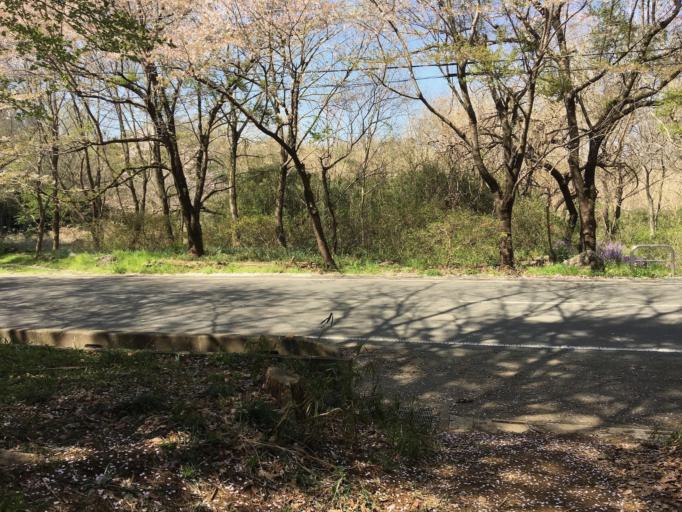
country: JP
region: Saitama
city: Morohongo
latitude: 35.9564
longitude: 139.3421
